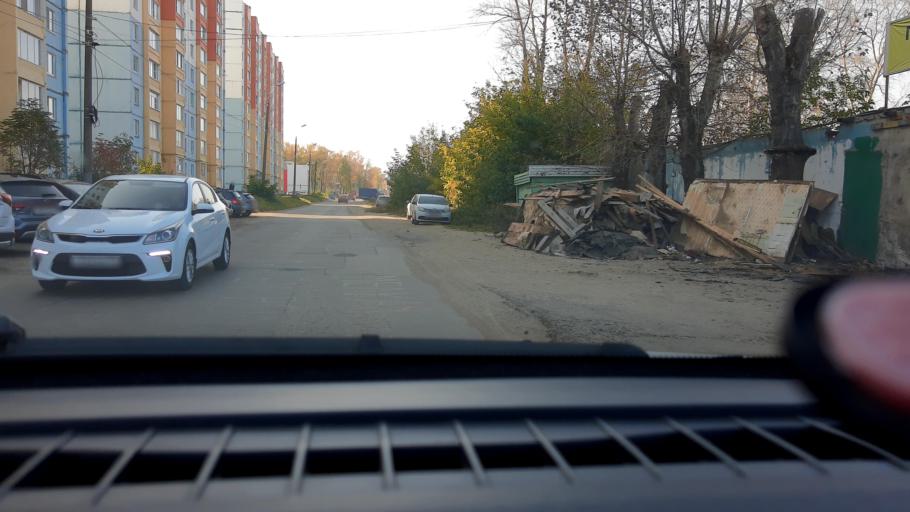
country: RU
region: Nizjnij Novgorod
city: Kstovo
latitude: 56.1556
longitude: 44.2073
